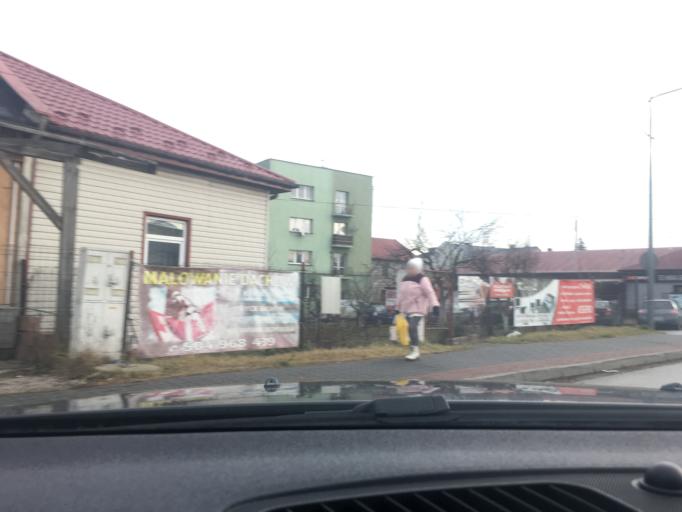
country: PL
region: Swietokrzyskie
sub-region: Powiat jedrzejowski
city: Jedrzejow
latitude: 50.6455
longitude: 20.2933
